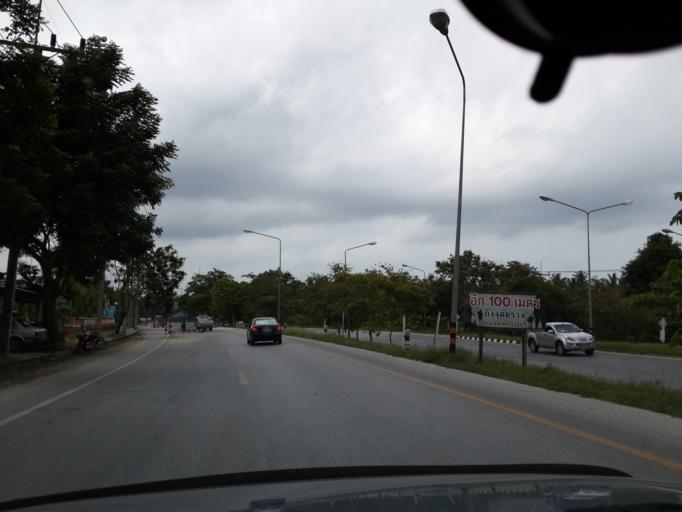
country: TH
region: Pattani
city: Pattani
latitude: 6.8732
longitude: 101.3002
